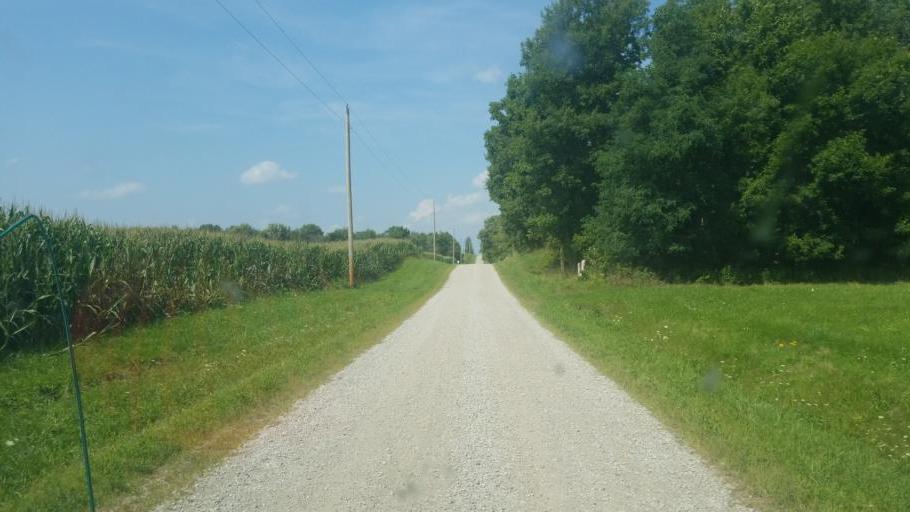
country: US
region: Ohio
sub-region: Huron County
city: New London
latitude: 41.0604
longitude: -82.4098
